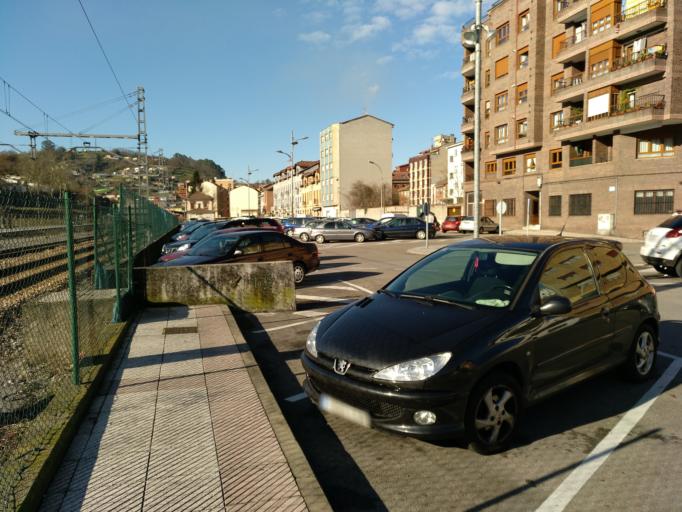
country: ES
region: Asturias
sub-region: Province of Asturias
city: Sama
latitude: 43.2910
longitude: -5.6774
